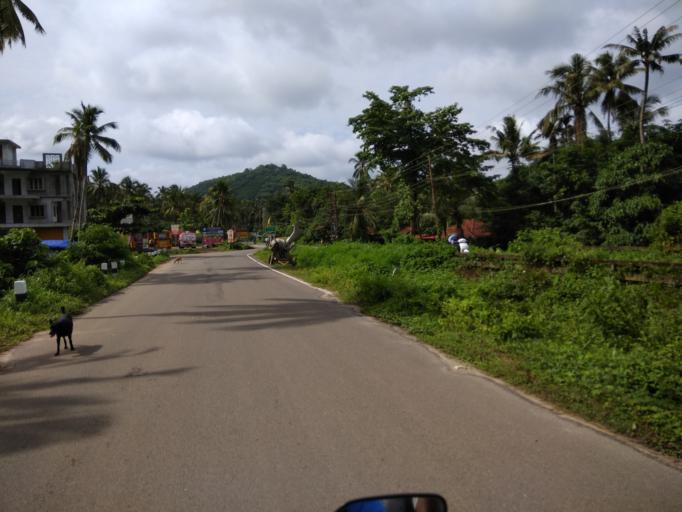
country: IN
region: Kerala
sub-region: Thrissur District
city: Trichur
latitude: 10.5369
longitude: 76.3344
